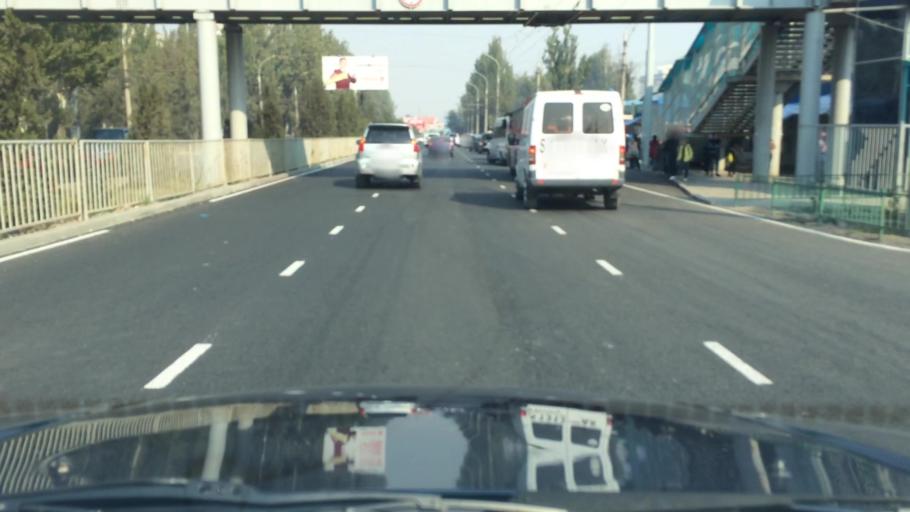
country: KG
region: Chuy
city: Lebedinovka
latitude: 42.8713
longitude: 74.6369
